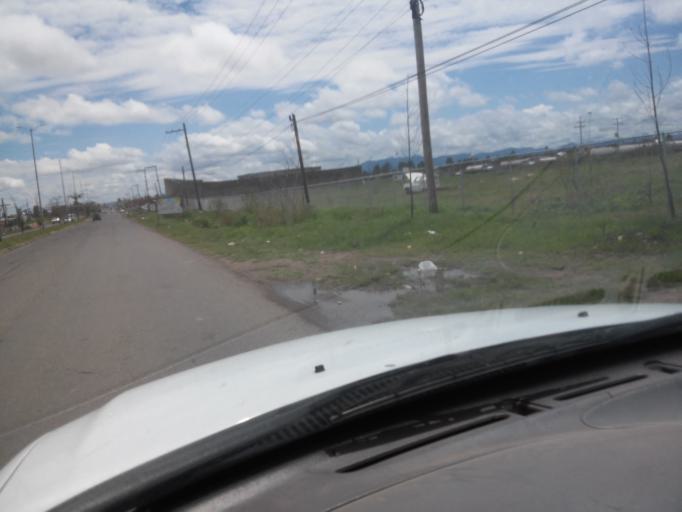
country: MX
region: Durango
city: Victoria de Durango
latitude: 24.0291
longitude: -104.6007
